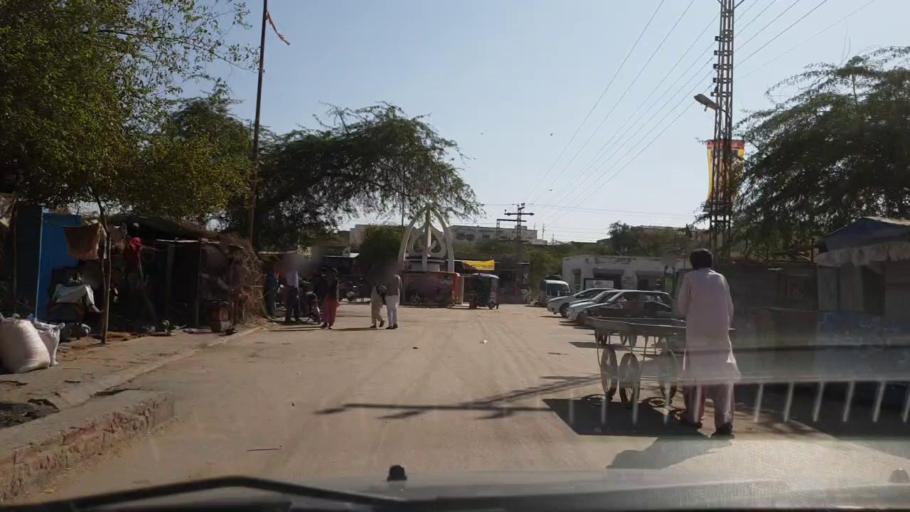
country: PK
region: Sindh
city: Diplo
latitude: 24.4696
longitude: 69.5793
